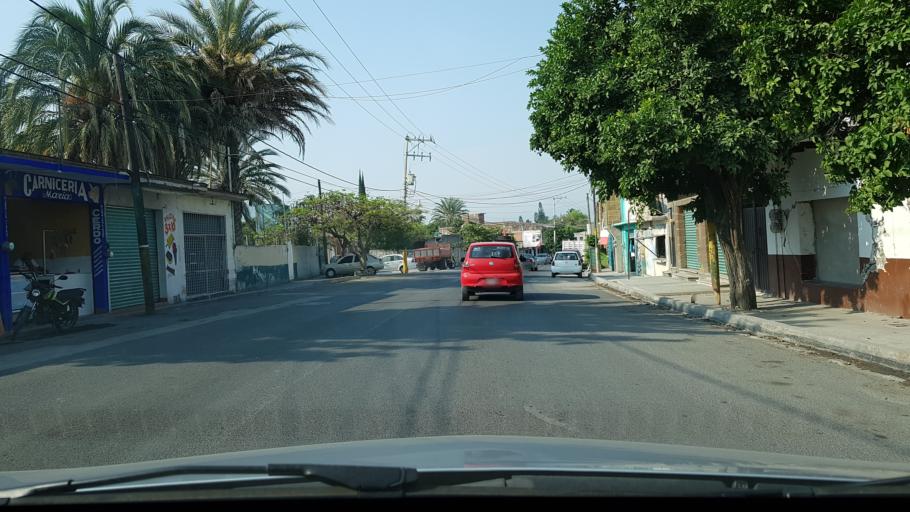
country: MX
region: Morelos
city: Tlaquiltenango
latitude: 18.6421
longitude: -99.1572
